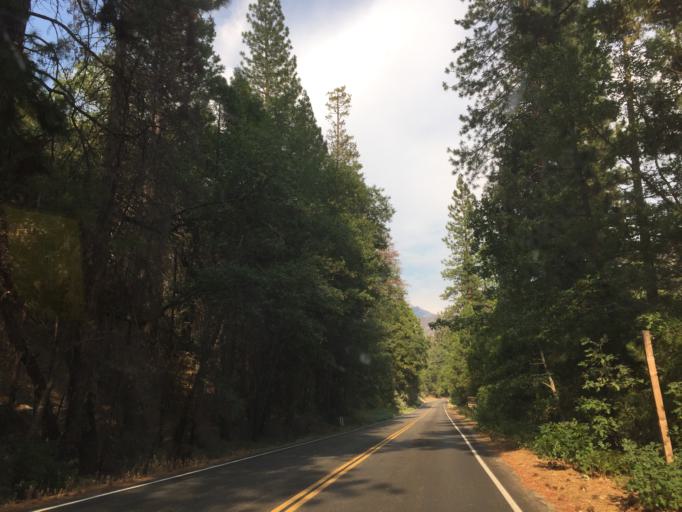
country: US
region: California
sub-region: Tulare County
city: Three Rivers
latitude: 36.8045
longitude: -118.7206
